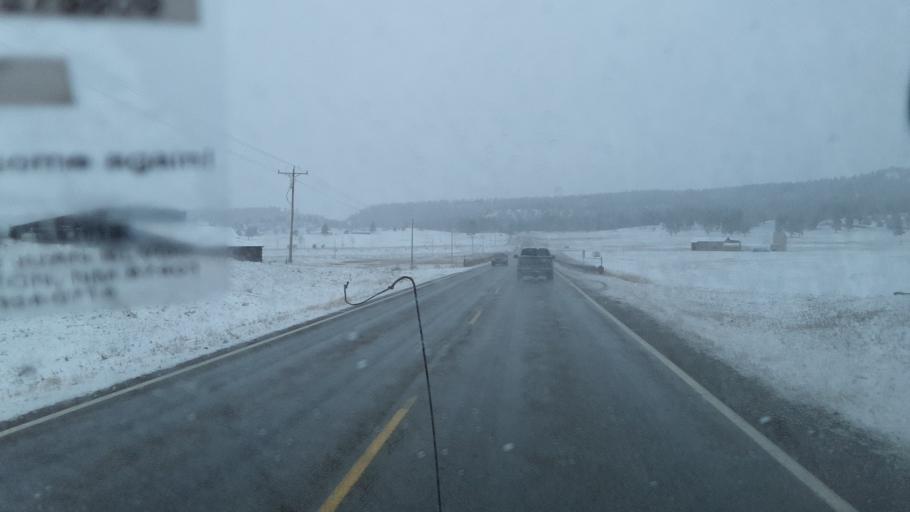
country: US
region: Colorado
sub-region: Archuleta County
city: Pagosa Springs
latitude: 37.1959
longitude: -106.9578
